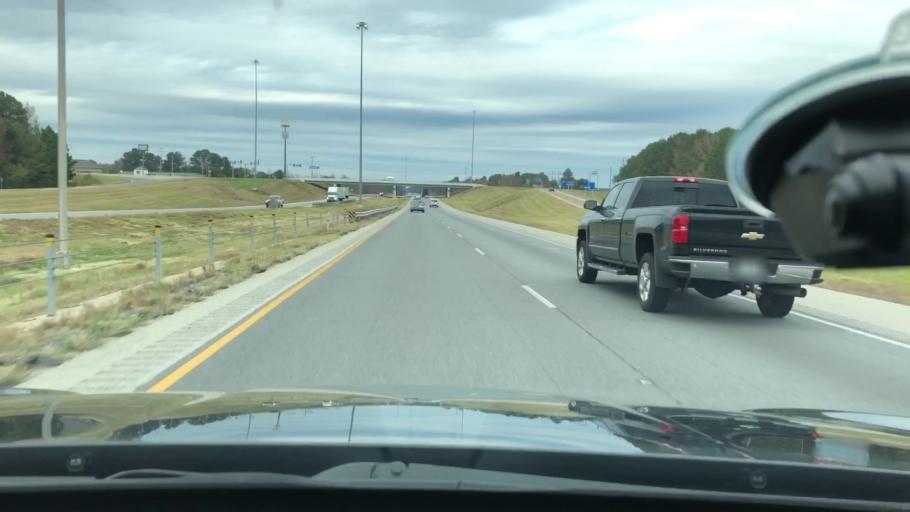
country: US
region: Arkansas
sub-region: Clark County
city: Arkadelphia
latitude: 34.1150
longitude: -93.0947
